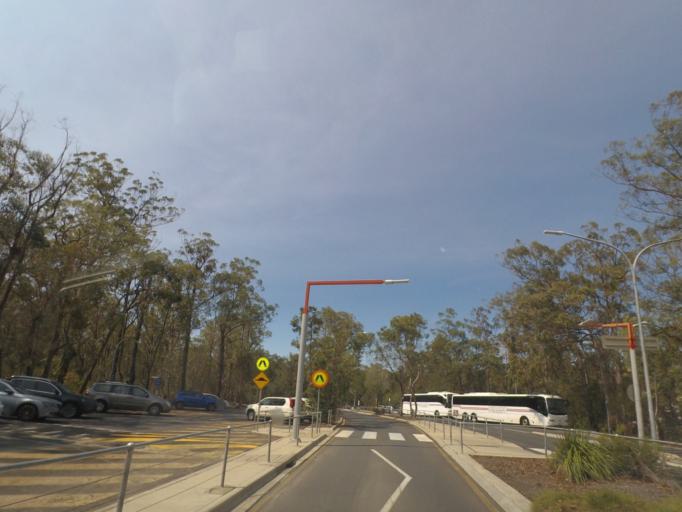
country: AU
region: Queensland
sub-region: Brisbane
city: Nathan
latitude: -27.5531
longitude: 153.0567
